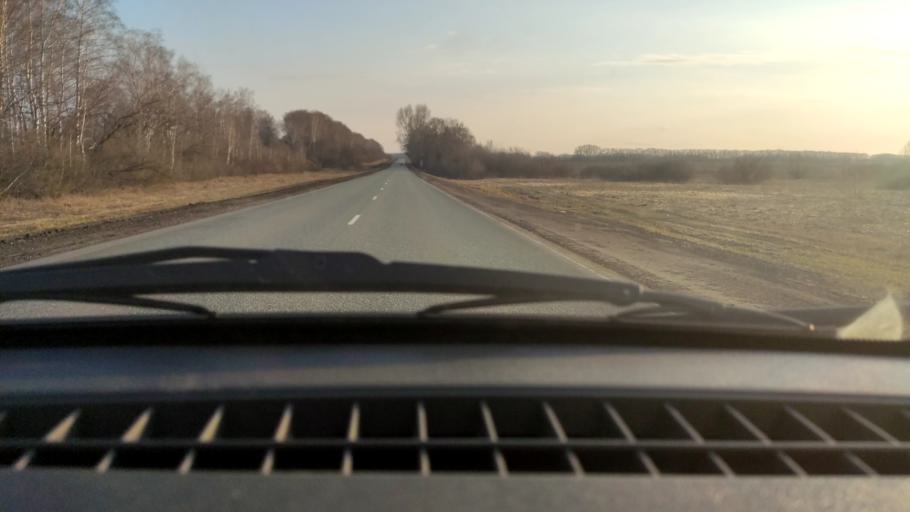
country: RU
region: Bashkortostan
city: Chishmy
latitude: 54.5365
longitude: 55.3133
